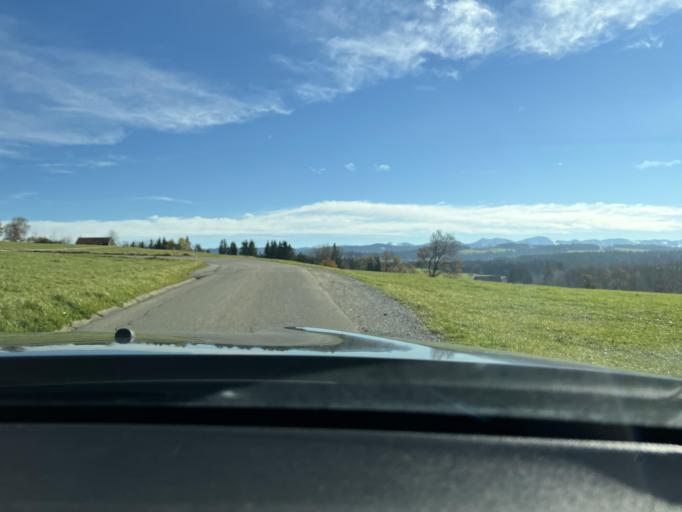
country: DE
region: Baden-Wuerttemberg
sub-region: Tuebingen Region
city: Isny im Allgau
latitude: 47.7123
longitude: 9.9970
